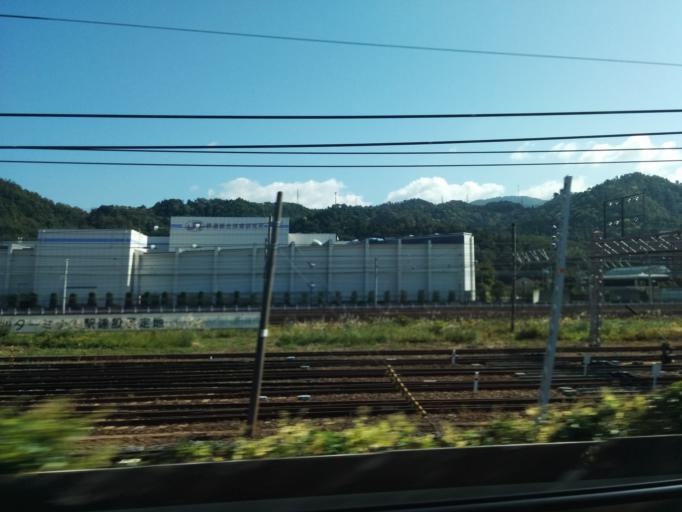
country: JP
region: Shiga Prefecture
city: Hikone
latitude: 35.3091
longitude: 136.2873
